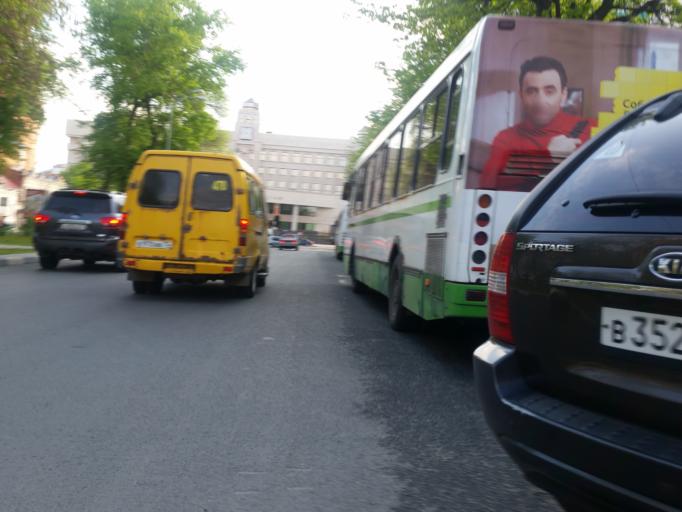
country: RU
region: Ulyanovsk
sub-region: Ulyanovskiy Rayon
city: Ulyanovsk
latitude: 54.3210
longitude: 48.4010
